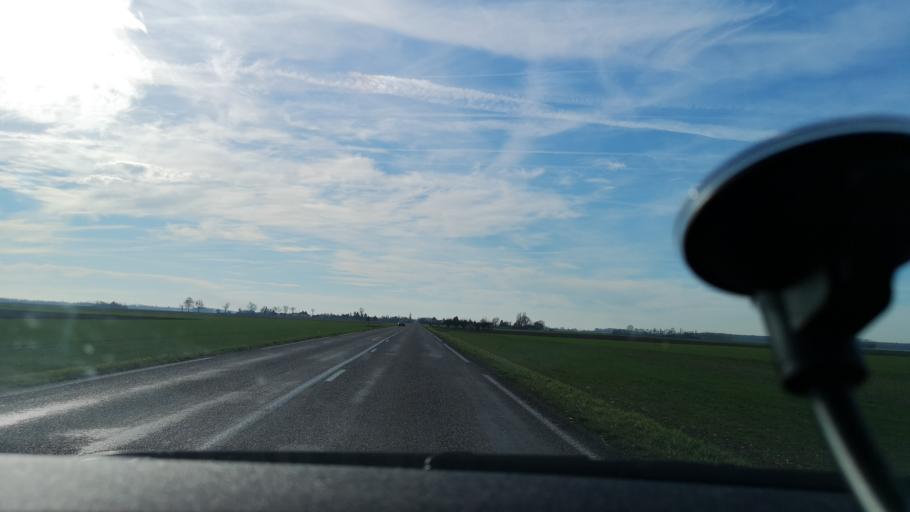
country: FR
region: Franche-Comte
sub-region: Departement du Jura
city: Petit-Noir
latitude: 46.9774
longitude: 5.3128
